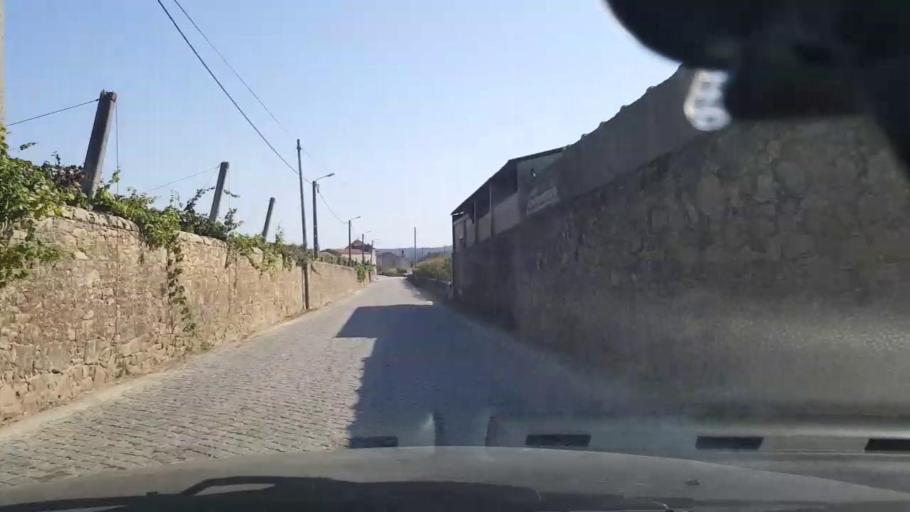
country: PT
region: Porto
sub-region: Povoa de Varzim
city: Pedroso
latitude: 41.4065
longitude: -8.6919
